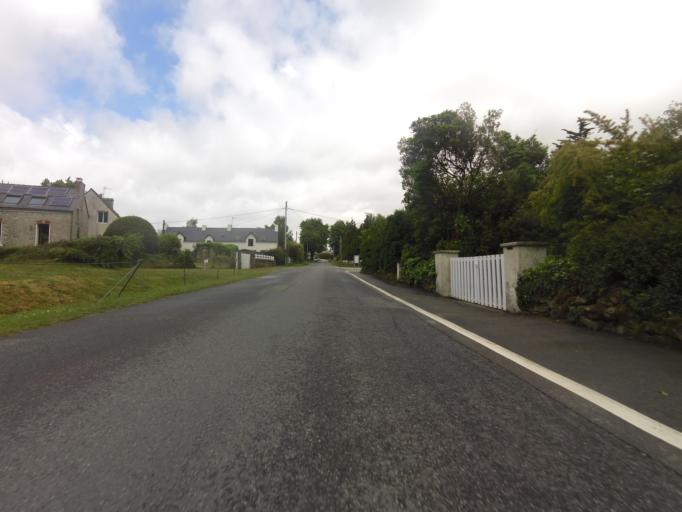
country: FR
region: Brittany
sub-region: Departement du Morbihan
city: Baden
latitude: 47.5987
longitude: -2.9121
